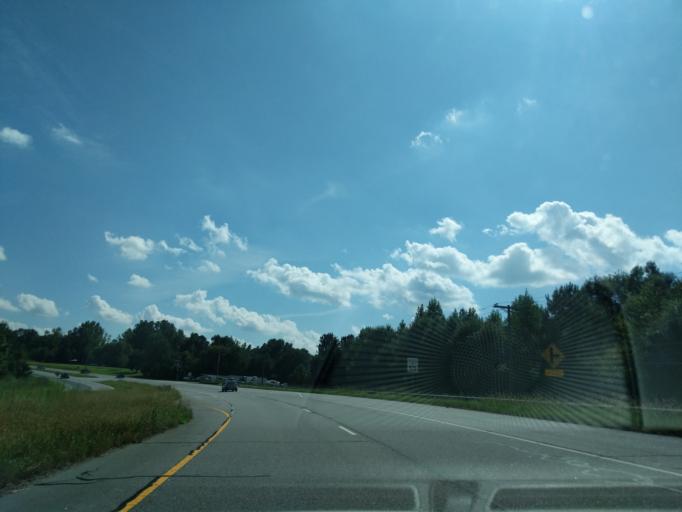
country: US
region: Georgia
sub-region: Jackson County
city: Commerce
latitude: 34.2688
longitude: -83.4684
